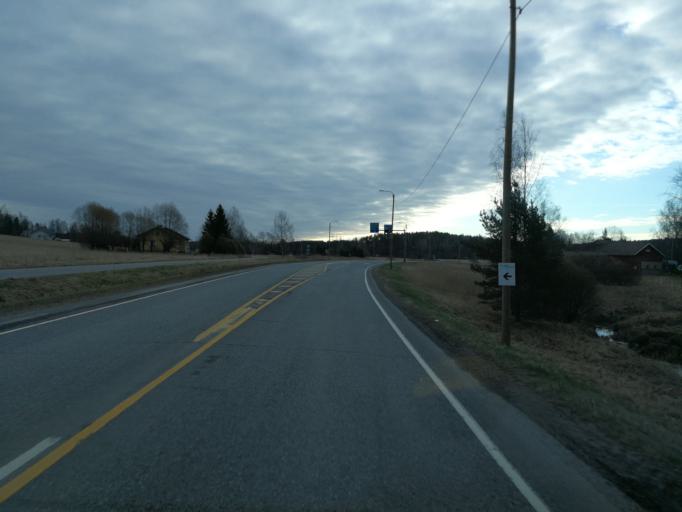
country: FI
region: Varsinais-Suomi
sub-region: Turku
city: Piikkioe
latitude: 60.4348
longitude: 22.5835
